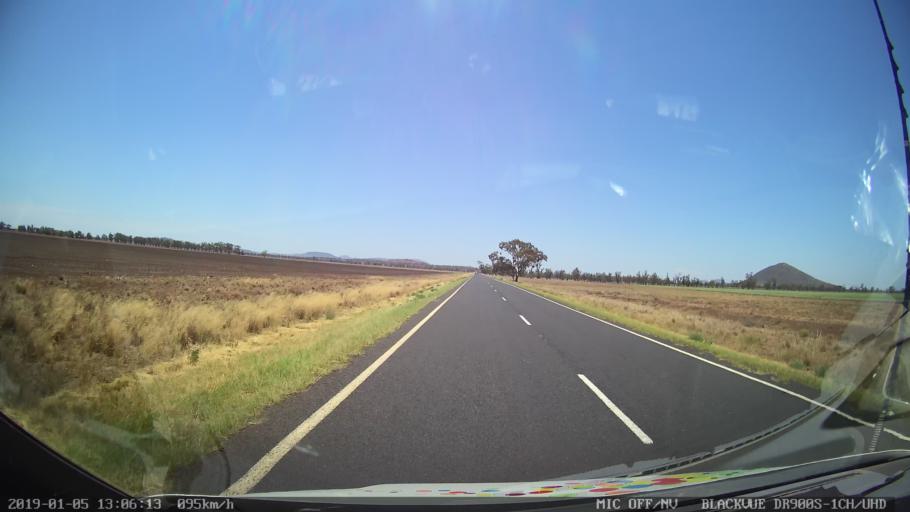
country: AU
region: New South Wales
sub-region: Gunnedah
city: Gunnedah
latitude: -31.0948
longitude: 149.8655
